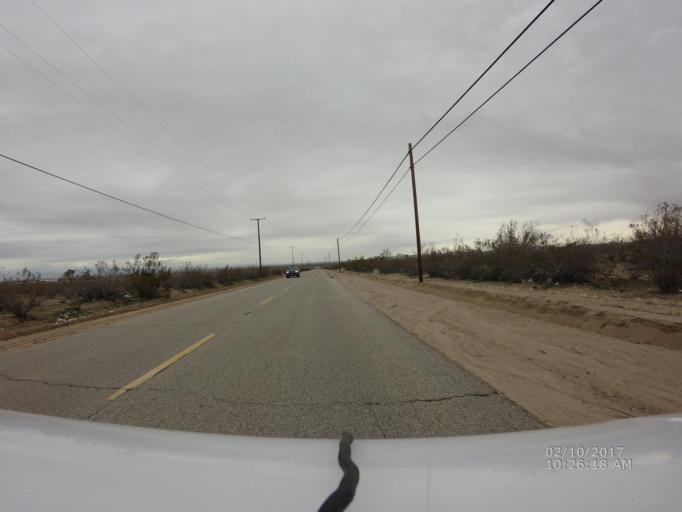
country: US
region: California
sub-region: Los Angeles County
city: Littlerock
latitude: 34.5171
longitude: -117.9405
